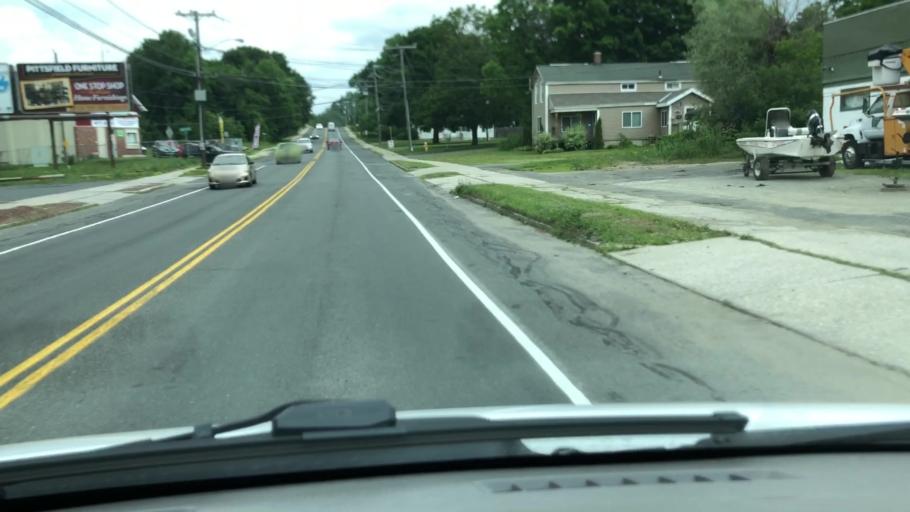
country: US
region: Massachusetts
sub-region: Berkshire County
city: Pittsfield
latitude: 42.4770
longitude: -73.2450
